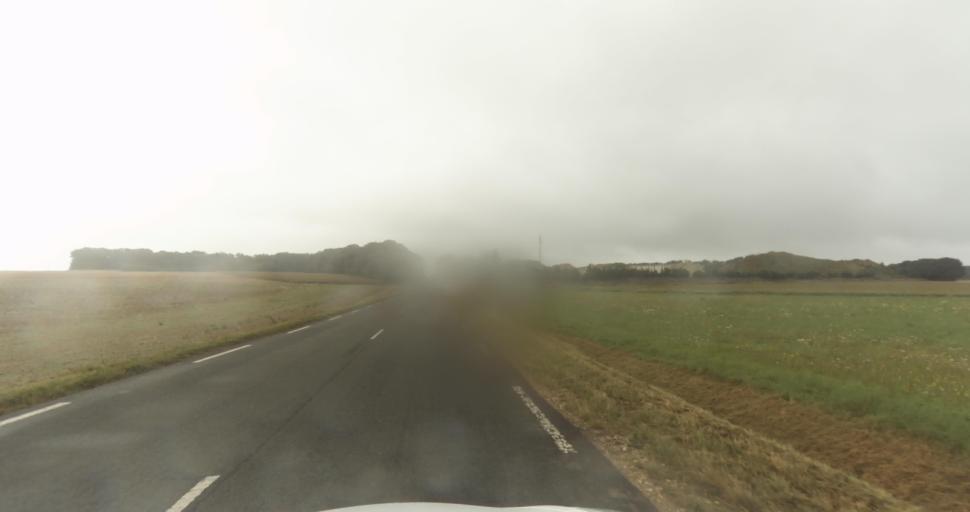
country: FR
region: Haute-Normandie
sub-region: Departement de l'Eure
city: Normanville
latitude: 49.0966
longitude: 1.1748
